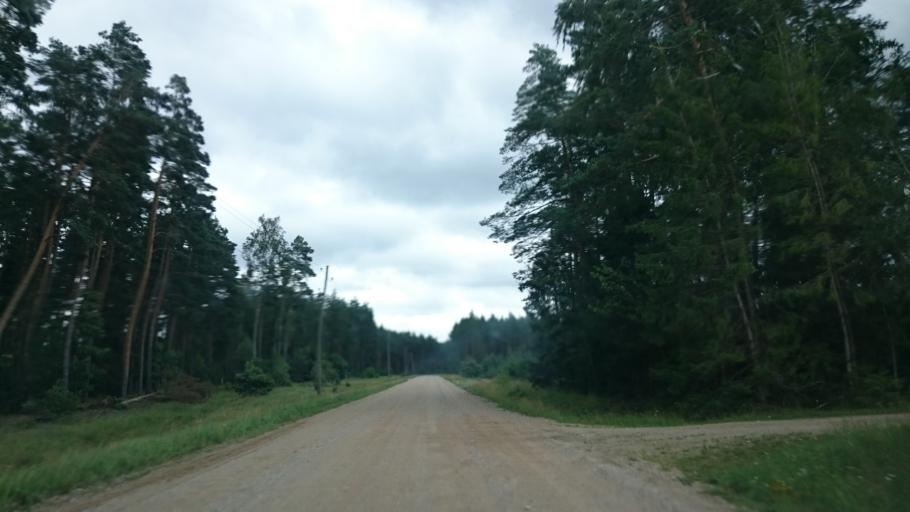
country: LV
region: Pavilostas
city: Pavilosta
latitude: 56.7677
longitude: 21.2914
